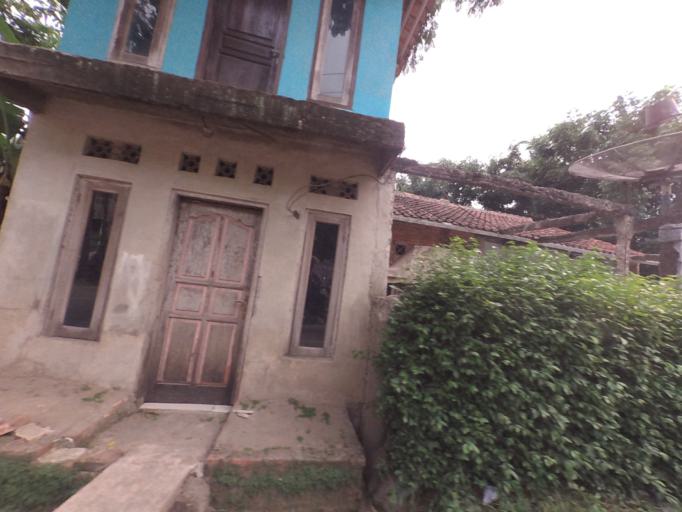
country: ID
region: West Java
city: Sidoger Lebak
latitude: -6.5625
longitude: 106.5806
